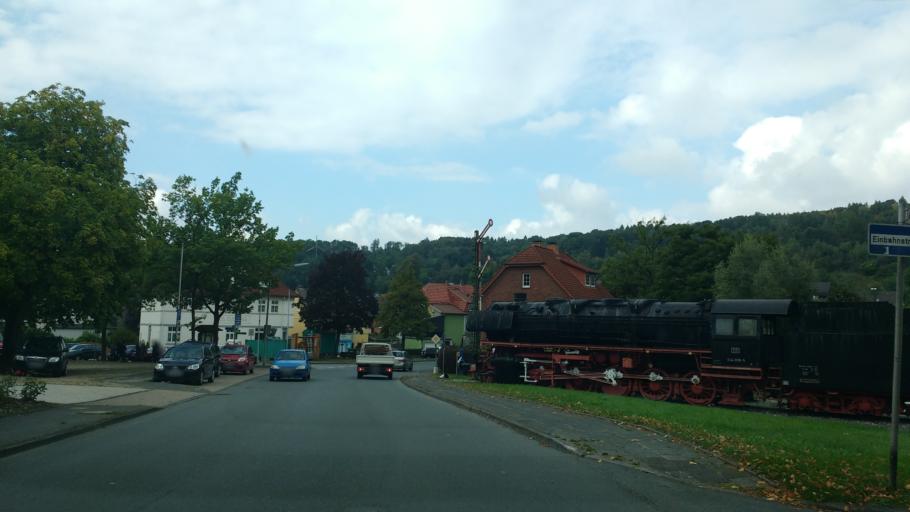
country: DE
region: North Rhine-Westphalia
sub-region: Regierungsbezirk Detmold
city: Altenbeken
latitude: 51.7626
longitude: 8.9362
